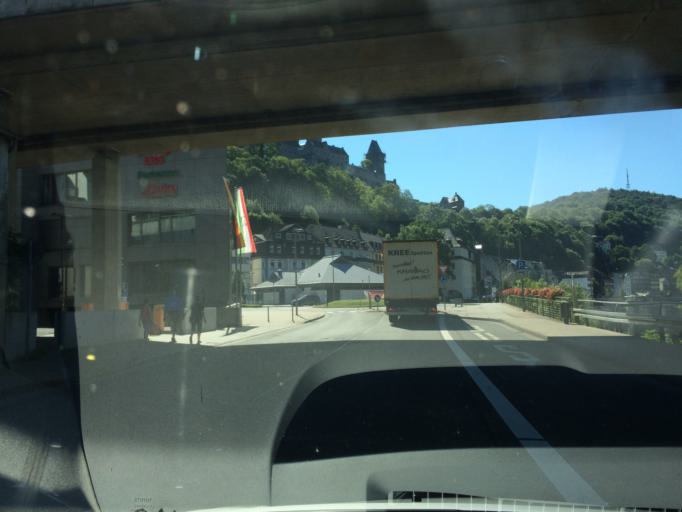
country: DE
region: North Rhine-Westphalia
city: Altena
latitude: 51.3020
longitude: 7.6707
